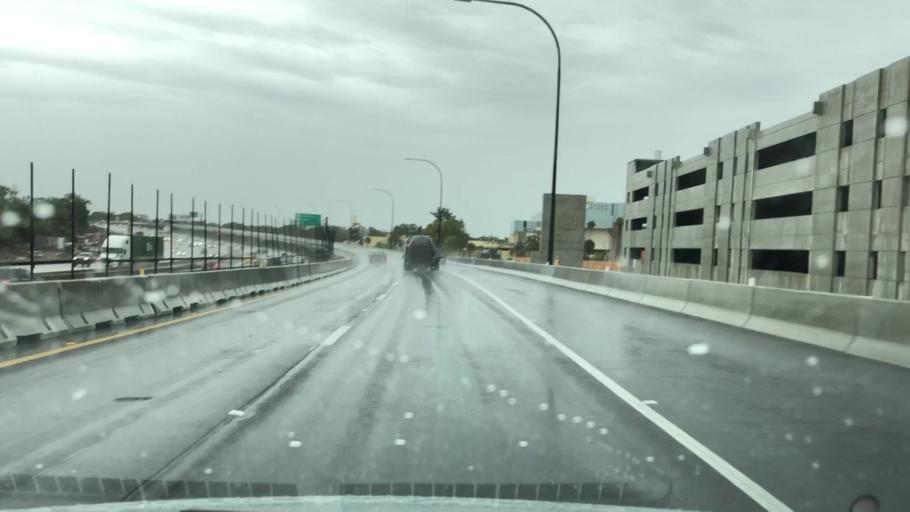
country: US
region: Florida
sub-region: Orange County
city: Fairview Shores
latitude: 28.5840
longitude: -81.3749
